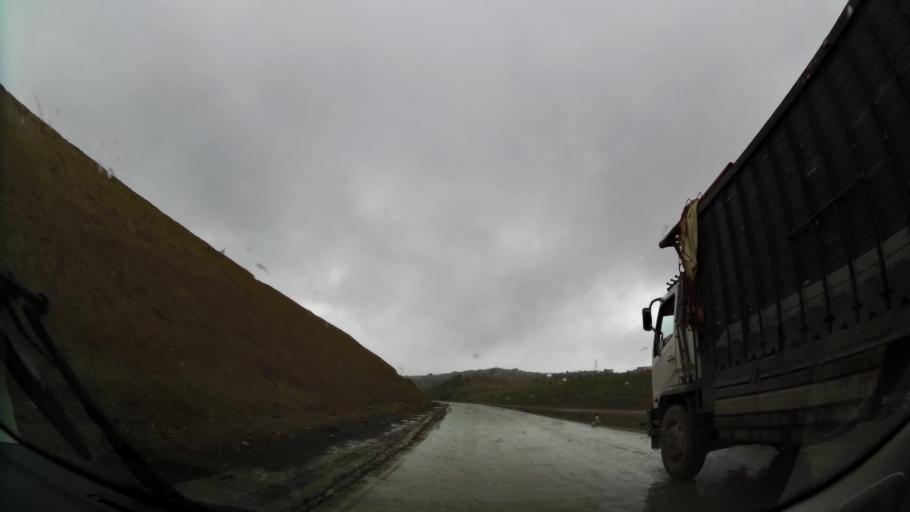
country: MA
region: Oriental
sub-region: Nador
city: Midar
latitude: 34.8886
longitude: -3.7542
